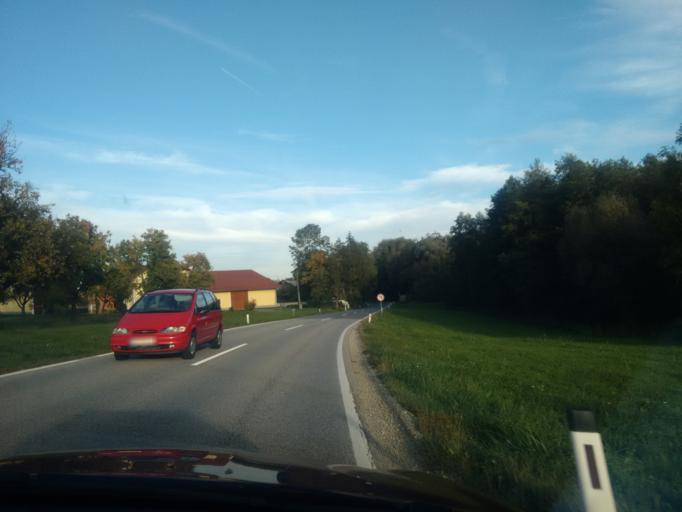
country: AT
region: Upper Austria
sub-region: Wels-Land
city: Bachmanning
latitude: 48.1764
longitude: 13.7719
